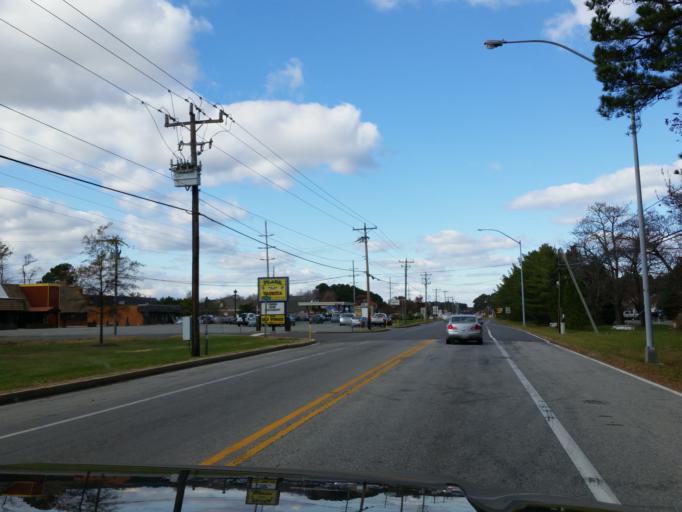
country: US
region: Maryland
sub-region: Talbot County
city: Saint Michaels
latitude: 38.7699
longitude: -76.2067
